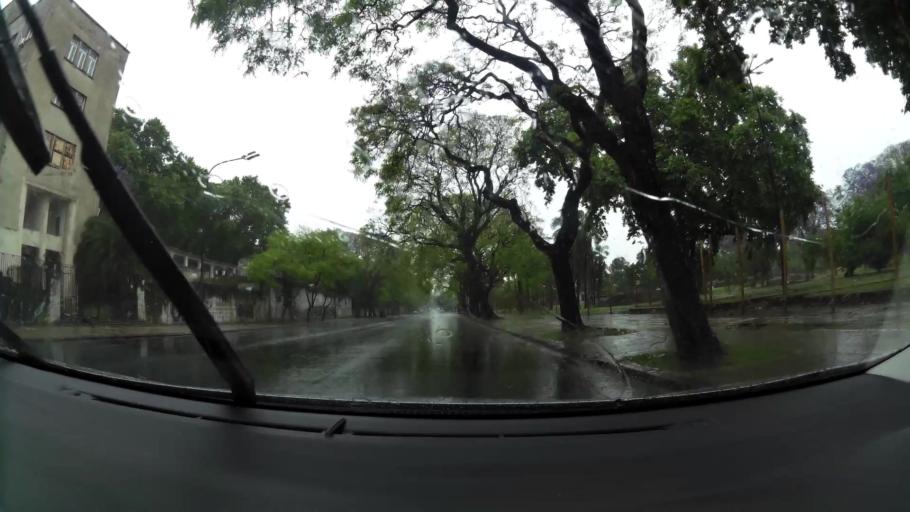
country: AR
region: Buenos Aires F.D.
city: Buenos Aires
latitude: -34.6343
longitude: -58.3845
